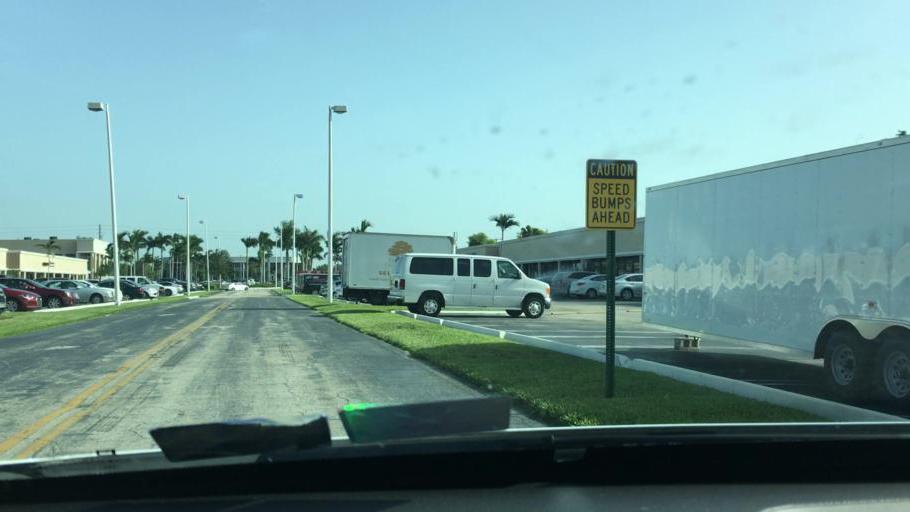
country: US
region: Florida
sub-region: Palm Beach County
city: Schall Circle
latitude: 26.7091
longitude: -80.1032
